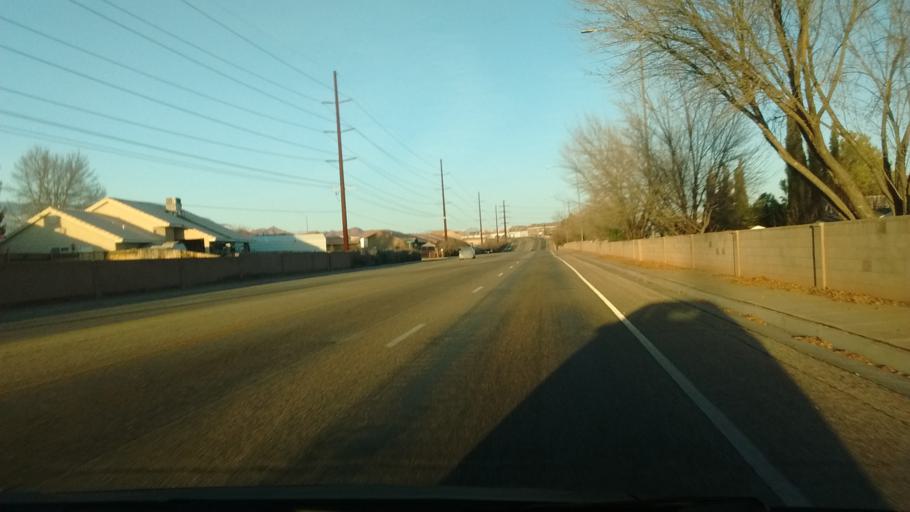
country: US
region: Utah
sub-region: Washington County
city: Washington
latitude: 37.1081
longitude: -113.5248
